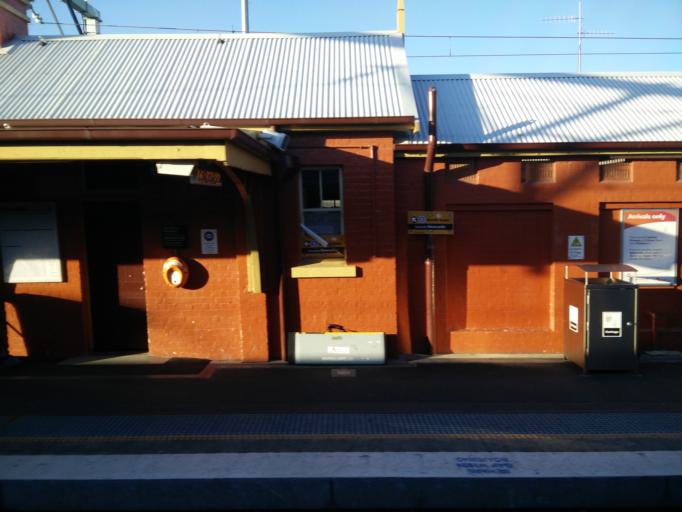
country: AU
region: New South Wales
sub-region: Newcastle
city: Hamilton
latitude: -32.9185
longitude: 151.7487
